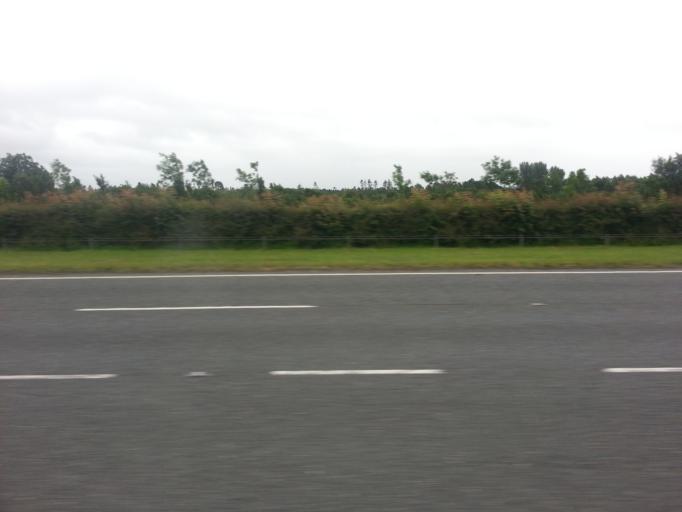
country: IE
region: Leinster
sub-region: Kildare
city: Kilcullen
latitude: 53.1756
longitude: -6.7452
